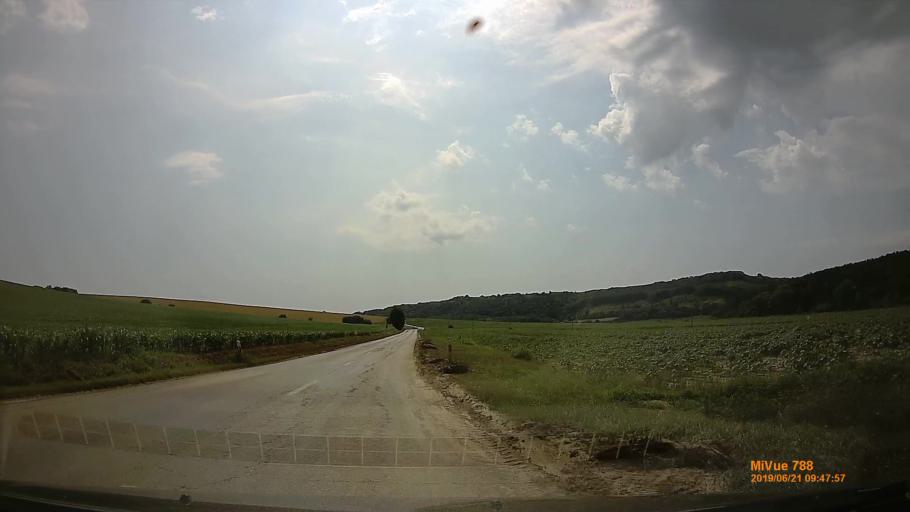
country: HU
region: Baranya
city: Sasd
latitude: 46.2693
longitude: 18.0196
